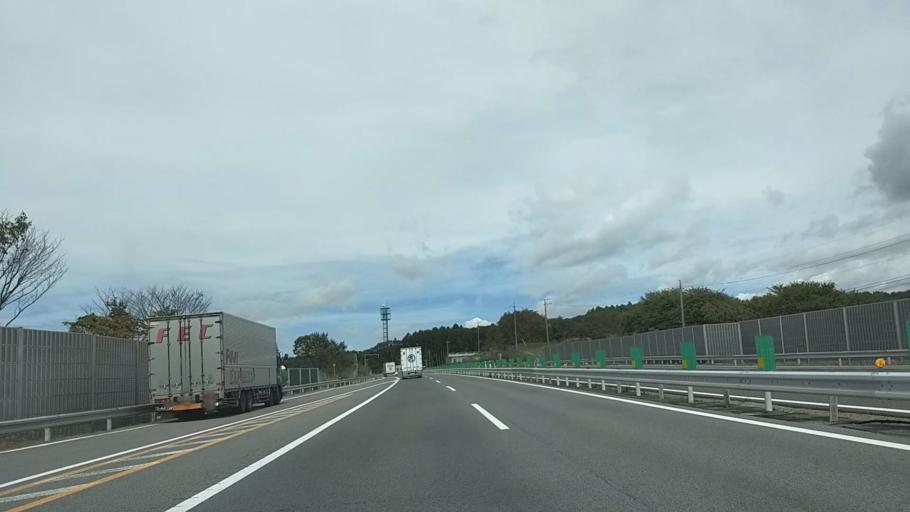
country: JP
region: Nagano
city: Chino
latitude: 35.9217
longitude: 138.2467
